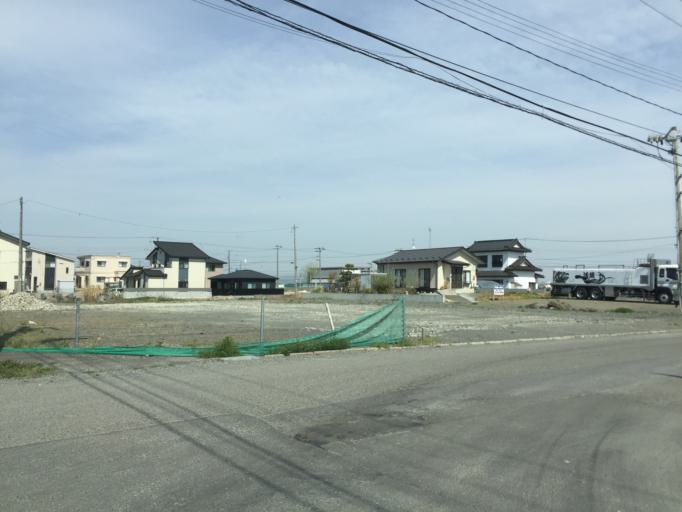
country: JP
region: Miyagi
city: Watari
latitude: 38.0401
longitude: 140.9118
